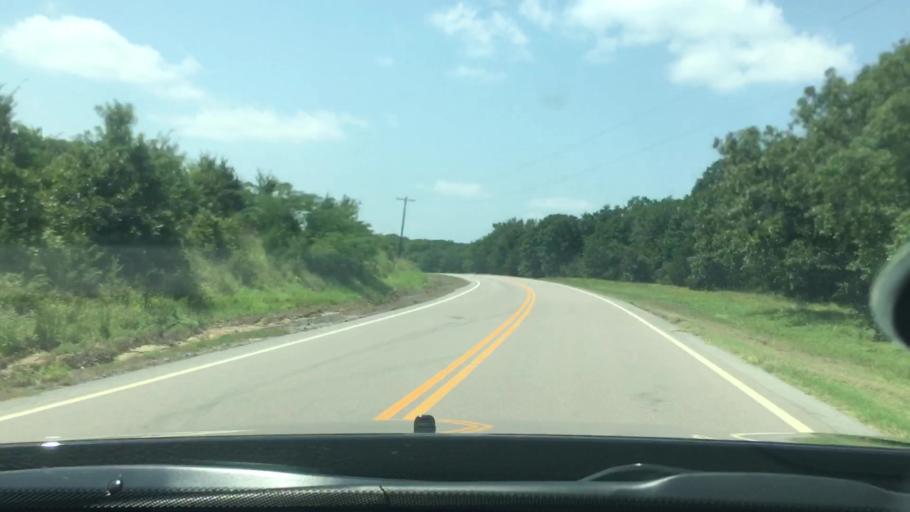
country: US
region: Oklahoma
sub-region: Coal County
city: Coalgate
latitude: 34.3744
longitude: -96.3902
